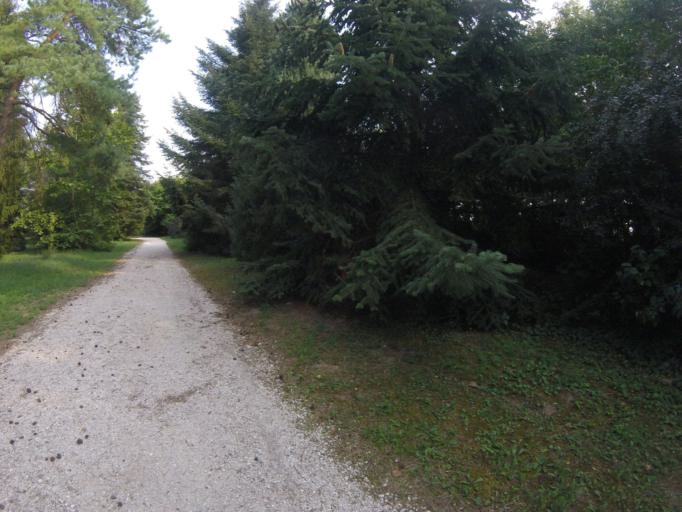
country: HU
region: Komarom-Esztergom
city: Babolna
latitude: 47.6412
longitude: 17.9875
